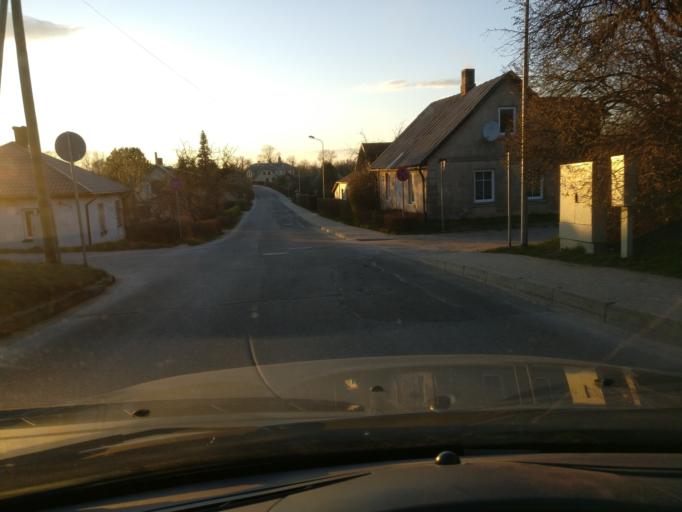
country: LV
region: Aluksnes Rajons
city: Aluksne
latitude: 57.4162
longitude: 27.0569
